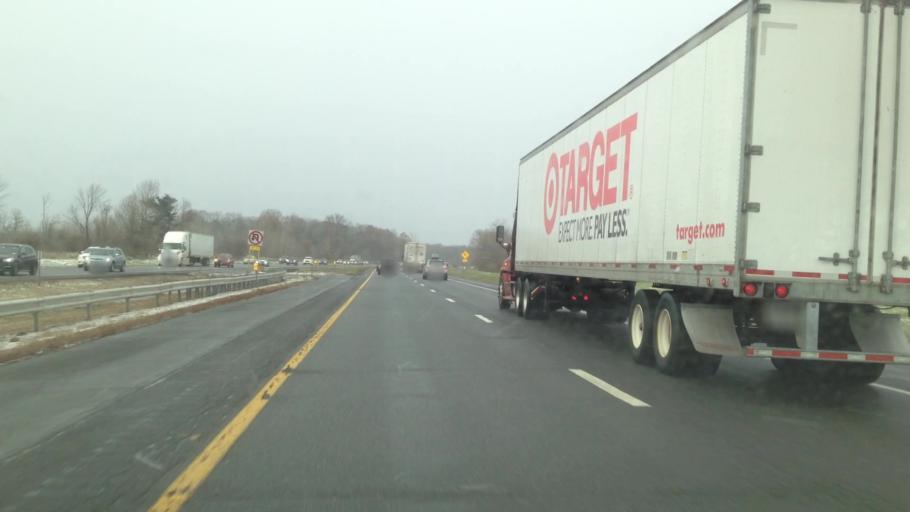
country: US
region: New York
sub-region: Rensselaer County
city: Castleton-on-Hudson
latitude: 42.5628
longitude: -73.7883
